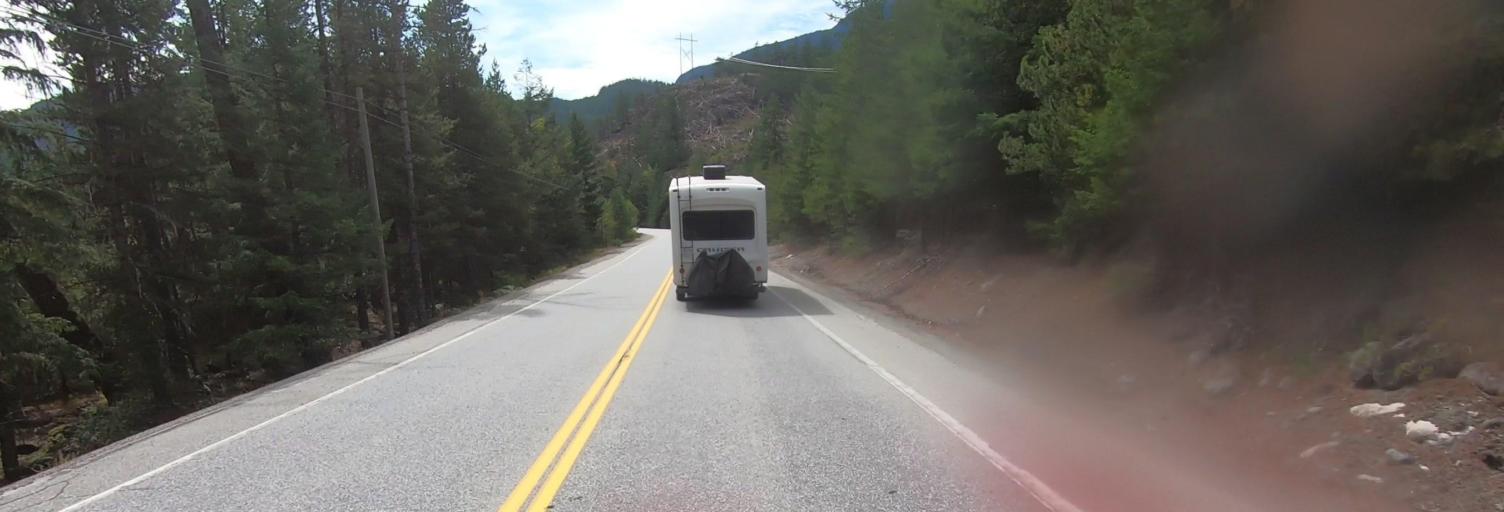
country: CA
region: British Columbia
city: Pemberton
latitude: 50.2759
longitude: -122.8664
